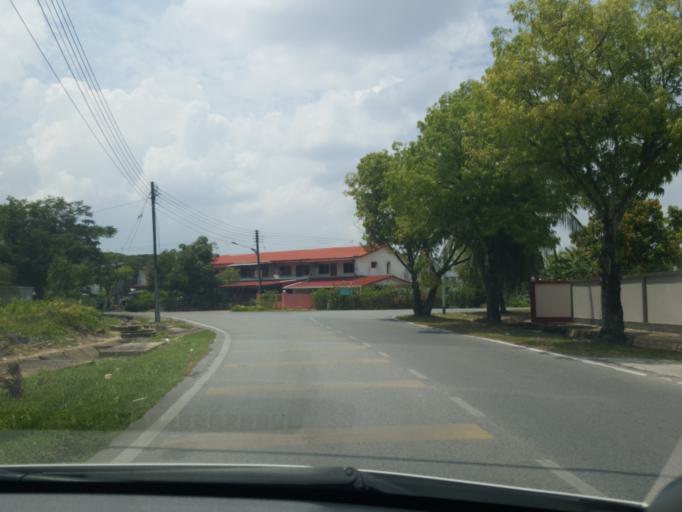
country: MY
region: Sarawak
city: Sarikei
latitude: 2.1234
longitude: 111.5249
